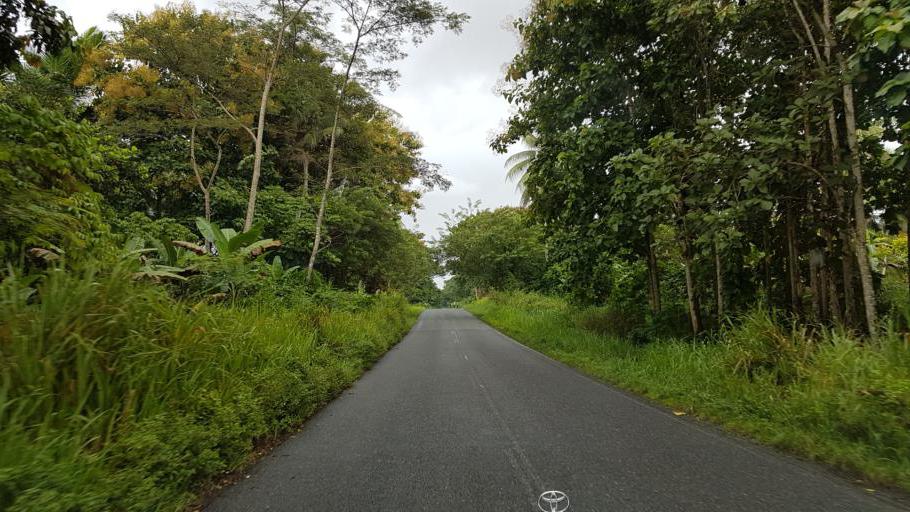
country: PG
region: Northern Province
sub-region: Sohe
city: Popondetta
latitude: -8.8222
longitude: 148.2594
